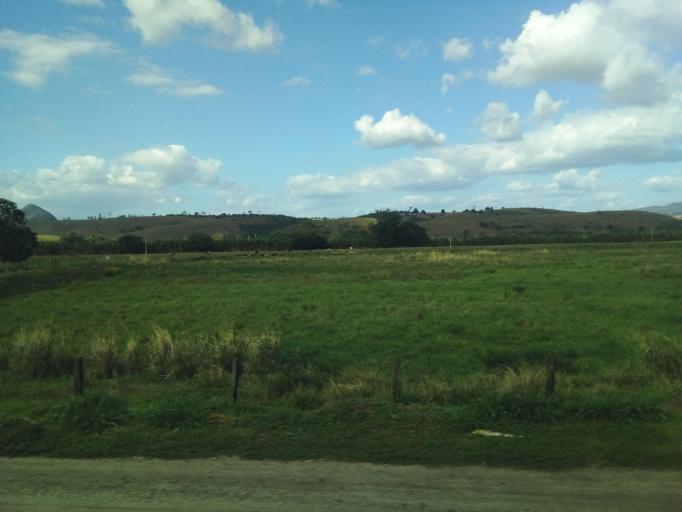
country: BR
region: Minas Gerais
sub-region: Conselheiro Pena
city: Conselheiro Pena
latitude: -18.9996
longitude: -41.5910
